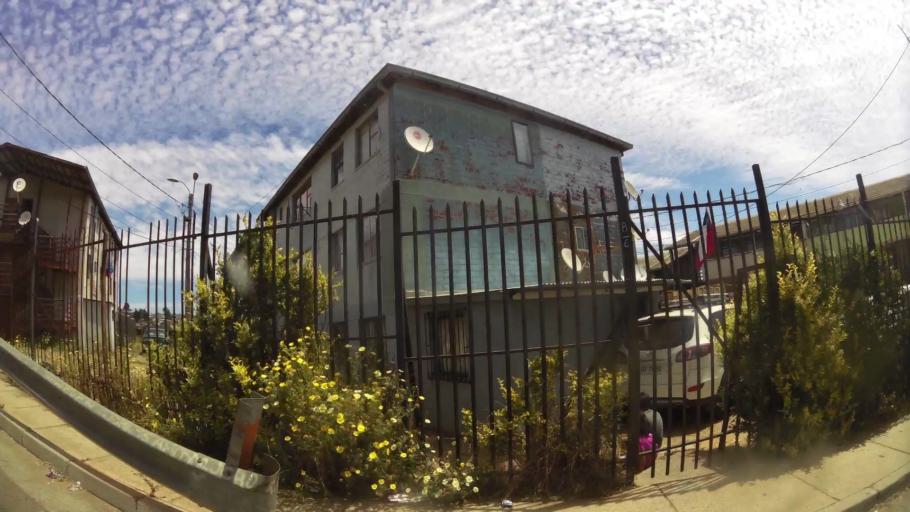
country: CL
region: Valparaiso
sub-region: Provincia de Valparaiso
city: Vina del Mar
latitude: -33.0543
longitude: -71.5735
